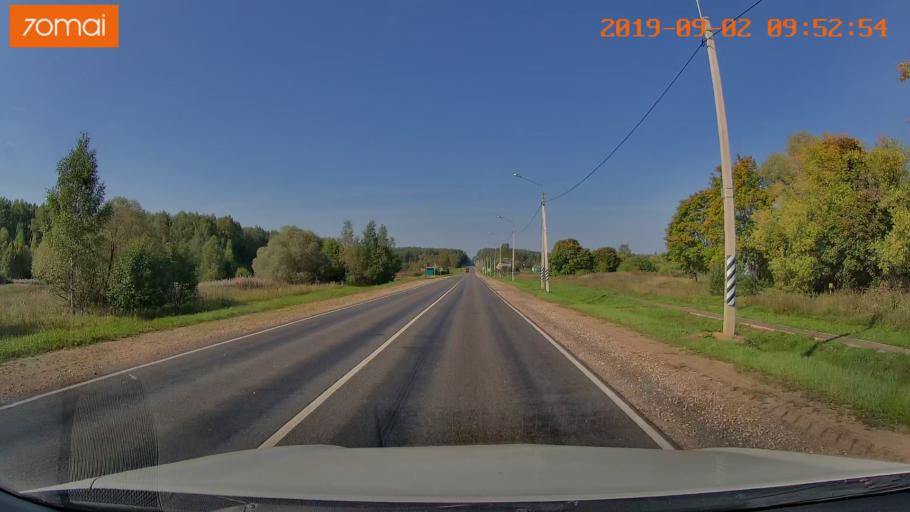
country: RU
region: Kaluga
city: Mosal'sk
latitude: 54.5860
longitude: 34.6886
